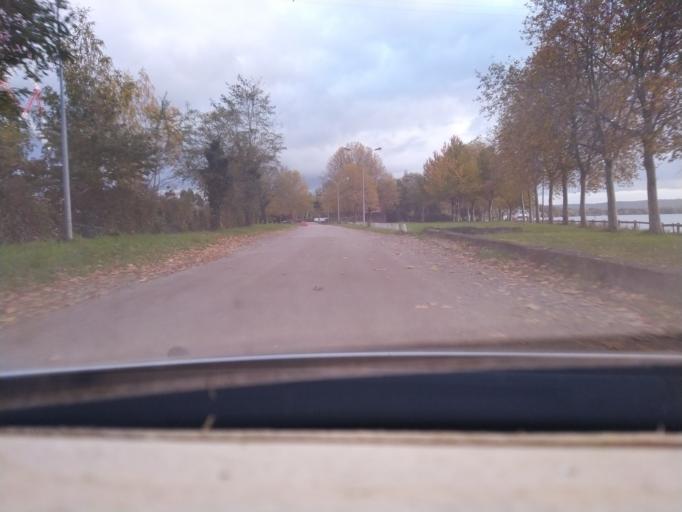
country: FR
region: Haute-Normandie
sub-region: Departement de la Seine-Maritime
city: Le Trait
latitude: 49.4595
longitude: 0.8189
